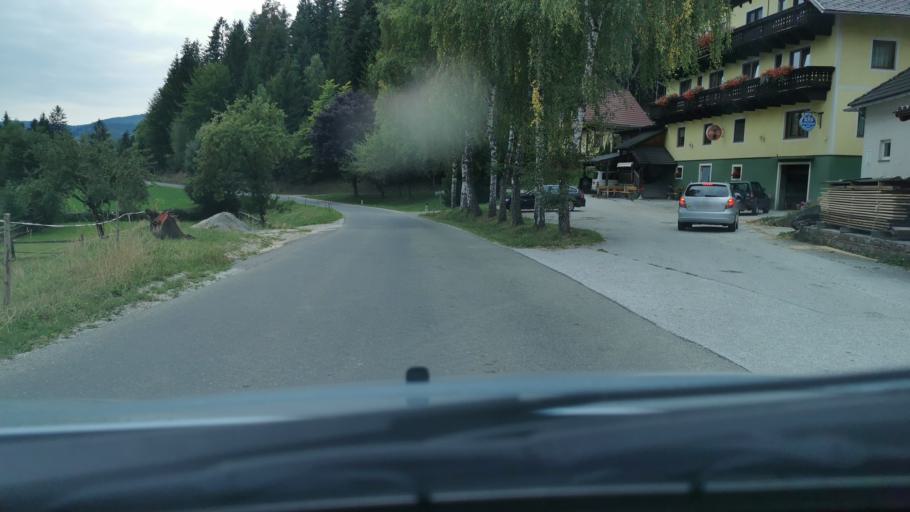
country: AT
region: Styria
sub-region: Politischer Bezirk Weiz
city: Strallegg
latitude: 47.3938
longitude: 15.6759
